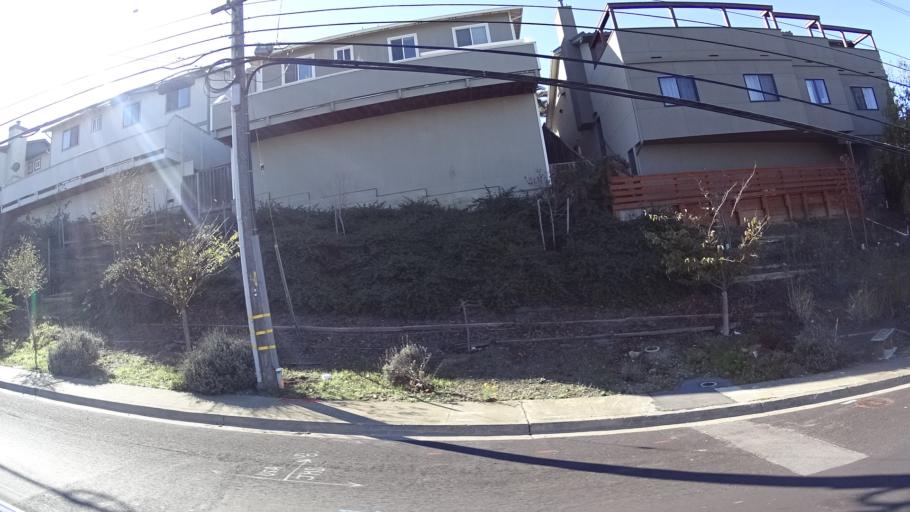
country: US
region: California
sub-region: San Mateo County
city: San Bruno
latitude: 37.6211
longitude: -122.4416
